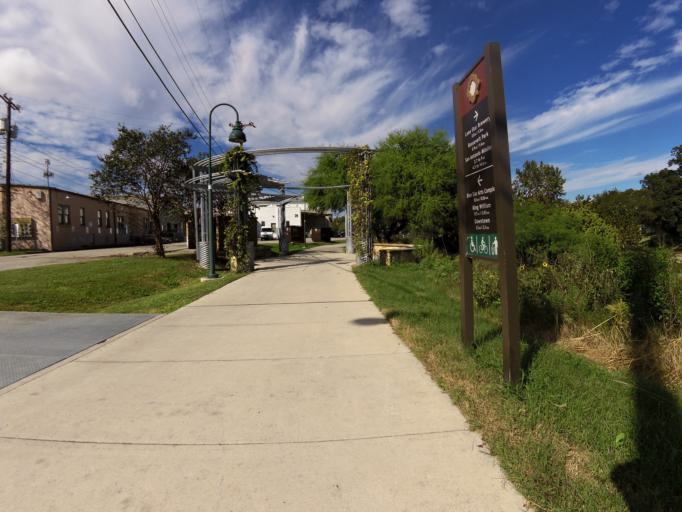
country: US
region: Texas
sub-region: Bexar County
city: San Antonio
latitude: 29.4076
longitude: -98.4951
